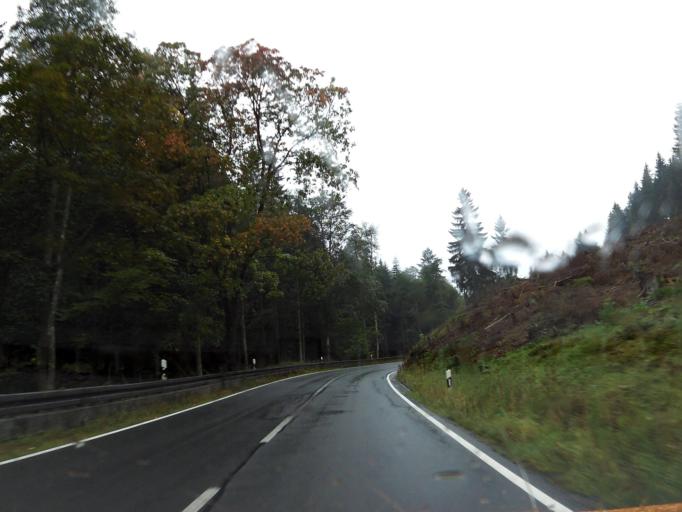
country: DE
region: Saxony-Anhalt
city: Hasselfelde
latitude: 51.6463
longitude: 10.8198
